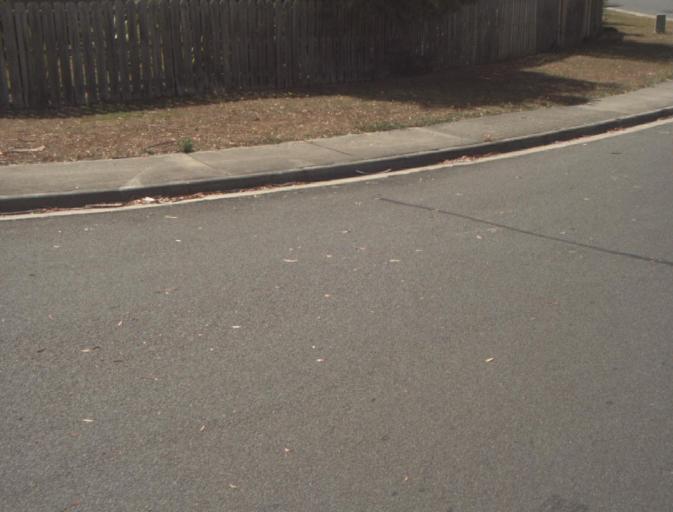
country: AU
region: Tasmania
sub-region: Launceston
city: Newstead
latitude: -41.4160
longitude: 147.1802
